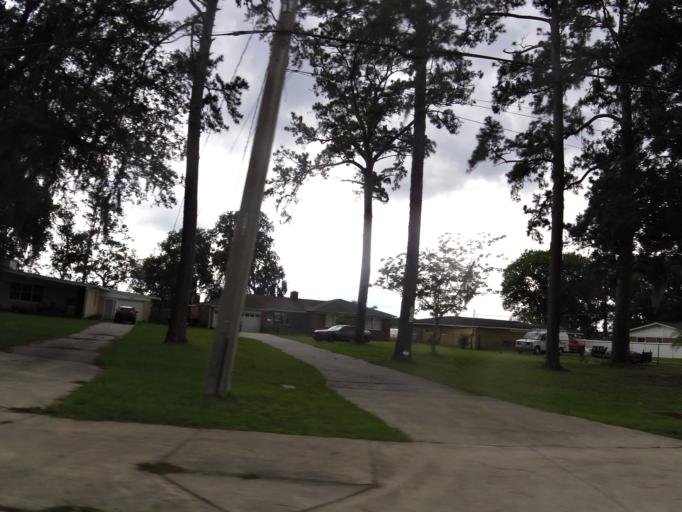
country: US
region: Florida
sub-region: Duval County
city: Jacksonville
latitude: 30.4230
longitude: -81.6740
